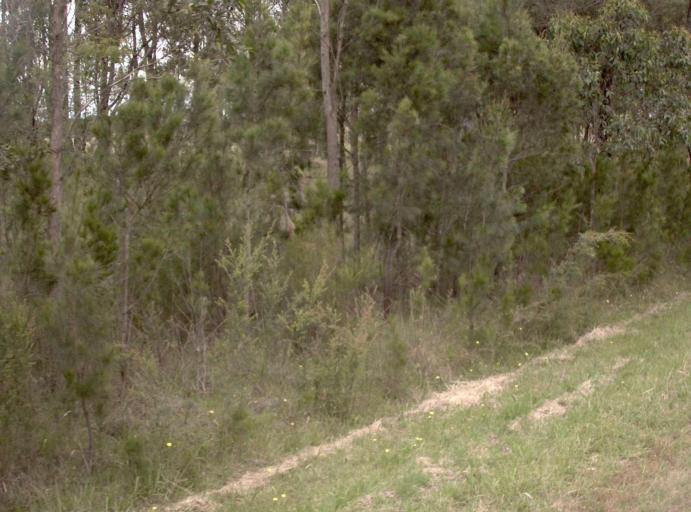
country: AU
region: Victoria
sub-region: Latrobe
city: Traralgon
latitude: -38.4789
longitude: 146.8214
